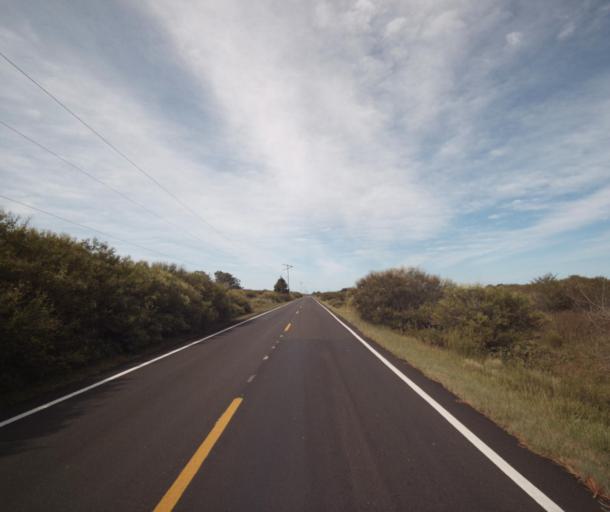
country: BR
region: Rio Grande do Sul
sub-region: Rio Grande
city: Rio Grande
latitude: -31.9144
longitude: -51.9397
